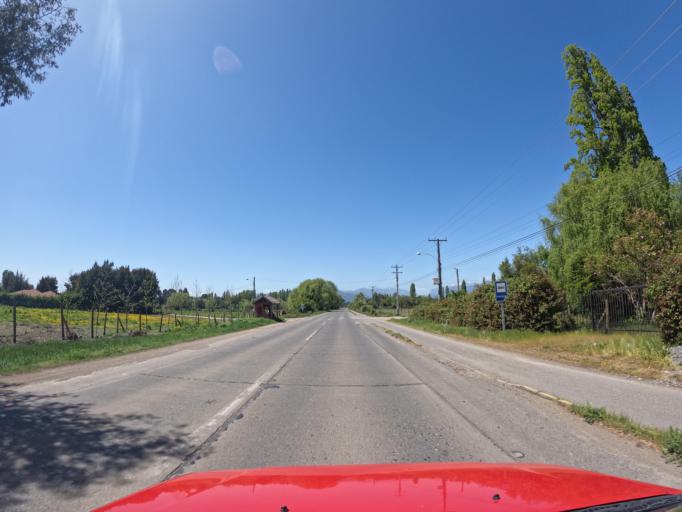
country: CL
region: Maule
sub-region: Provincia de Linares
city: Linares
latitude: -35.8290
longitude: -71.5031
